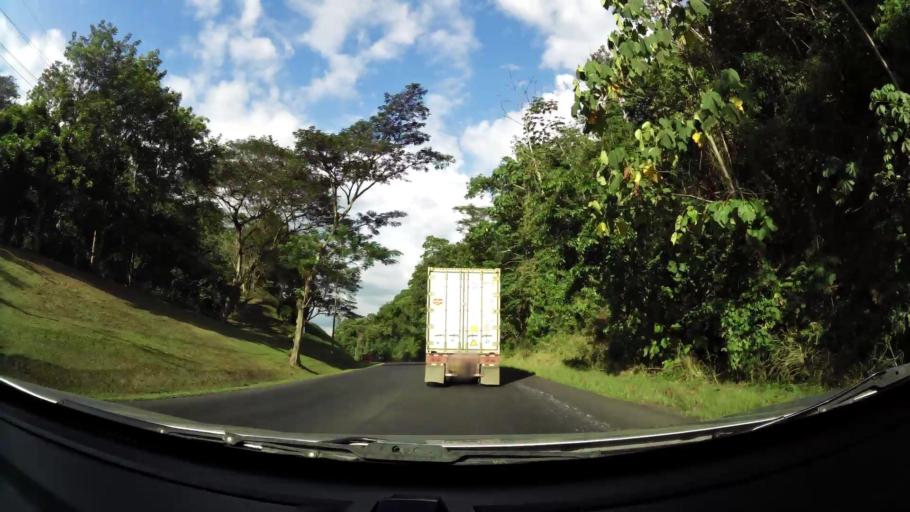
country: CR
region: Puntarenas
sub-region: Canton de Garabito
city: Jaco
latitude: 9.7676
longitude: -84.6113
